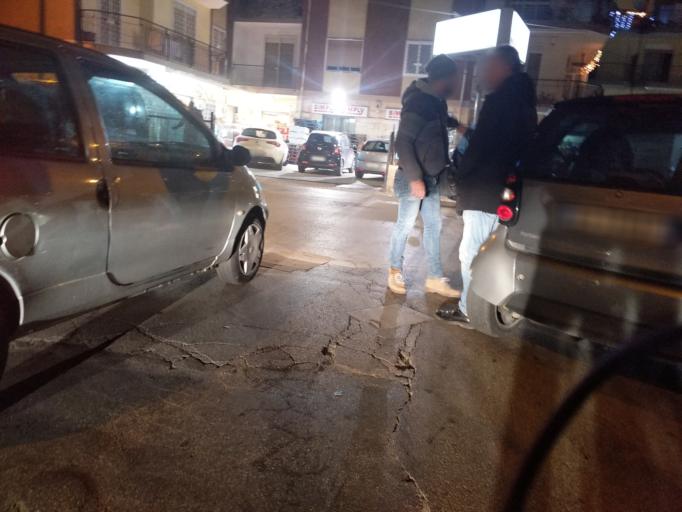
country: IT
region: Apulia
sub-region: Provincia di Bari
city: Modugno
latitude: 41.0843
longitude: 16.7884
